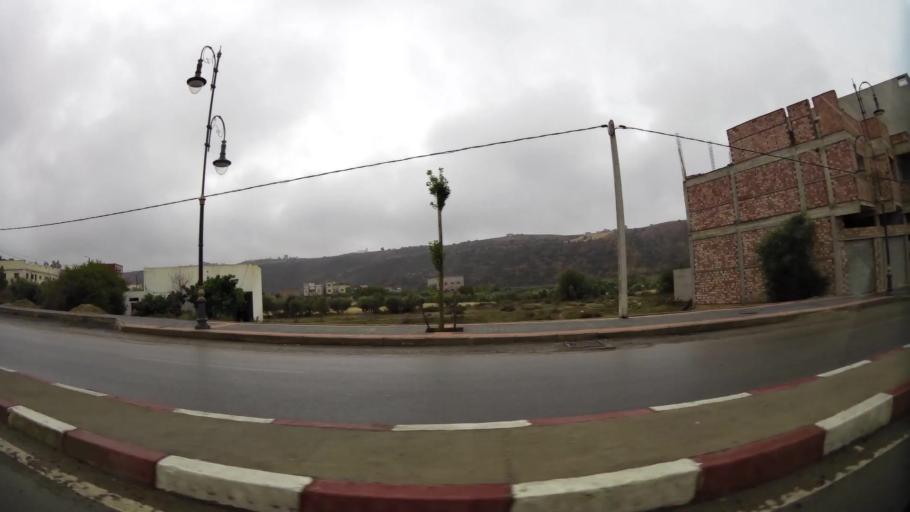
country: MA
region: Taza-Al Hoceima-Taounate
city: Imzourene
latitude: 35.1781
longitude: -3.8793
